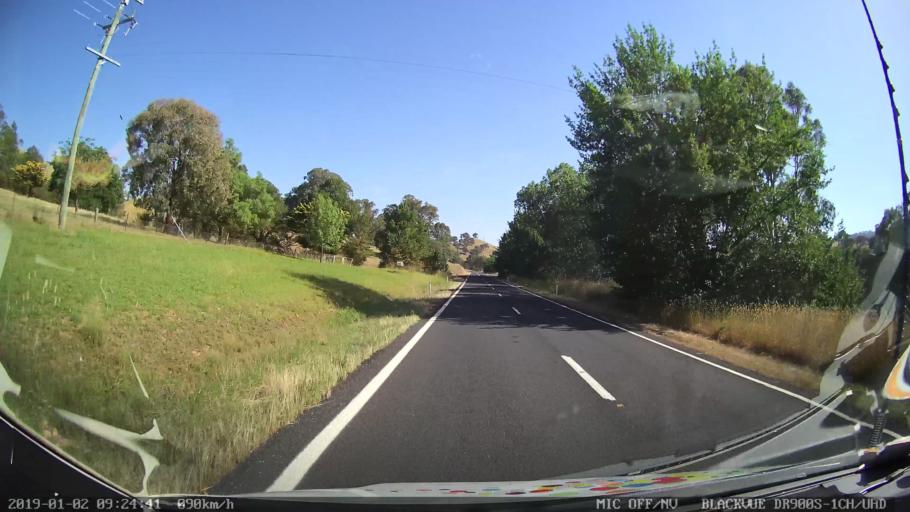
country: AU
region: New South Wales
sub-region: Tumut Shire
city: Tumut
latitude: -35.3739
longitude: 148.2917
